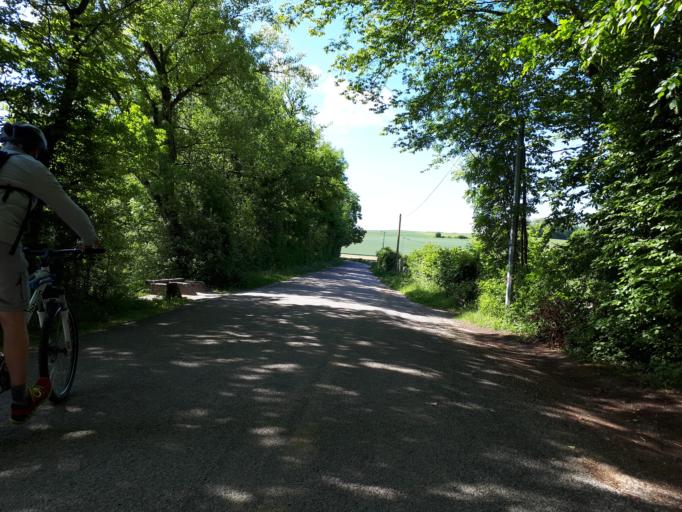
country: FR
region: Rhone-Alpes
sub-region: Departement de l'Isere
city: Saint-Chef
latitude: 45.5982
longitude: 5.3554
